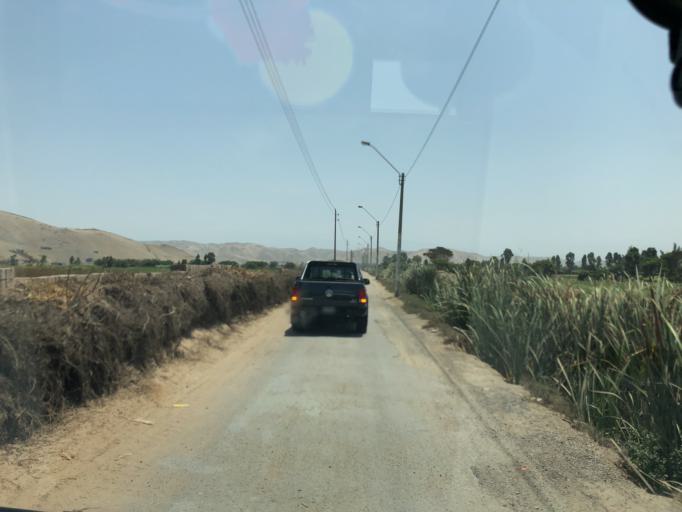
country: PE
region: Lima
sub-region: Provincia de Canete
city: San Vicente de Canete
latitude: -13.0231
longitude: -76.4710
